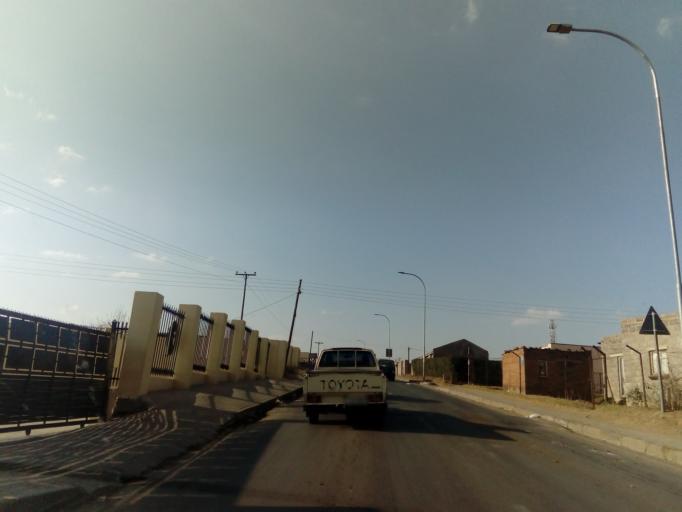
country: LS
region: Maseru
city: Maseru
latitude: -29.3037
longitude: 27.5340
